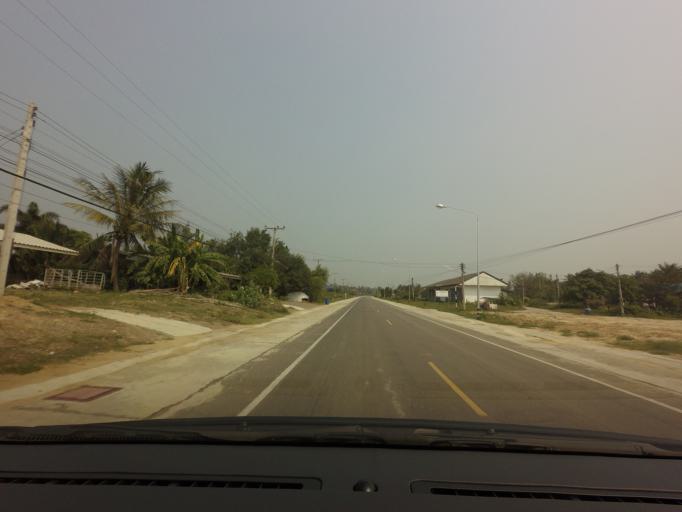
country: TH
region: Prachuap Khiri Khan
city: Kui Buri
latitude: 12.0641
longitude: 99.8886
